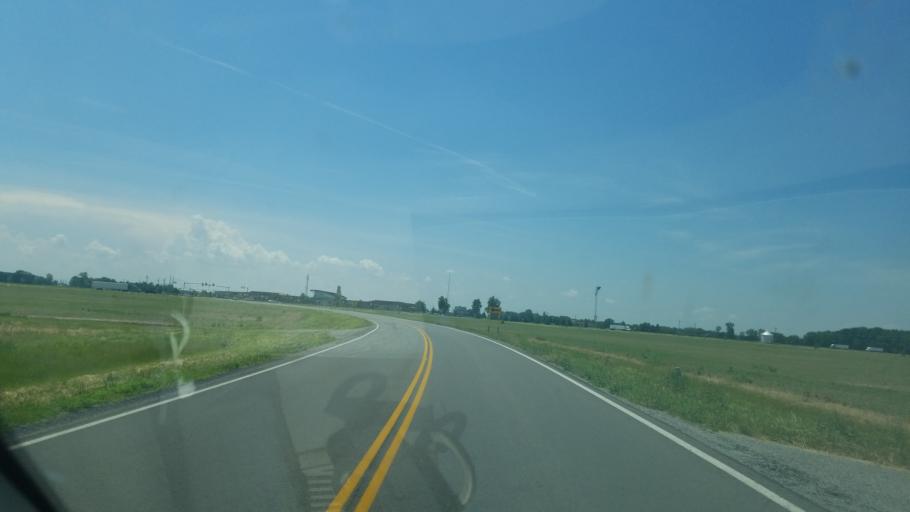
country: US
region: Ohio
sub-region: Hancock County
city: Findlay
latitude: 41.0841
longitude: -83.6173
